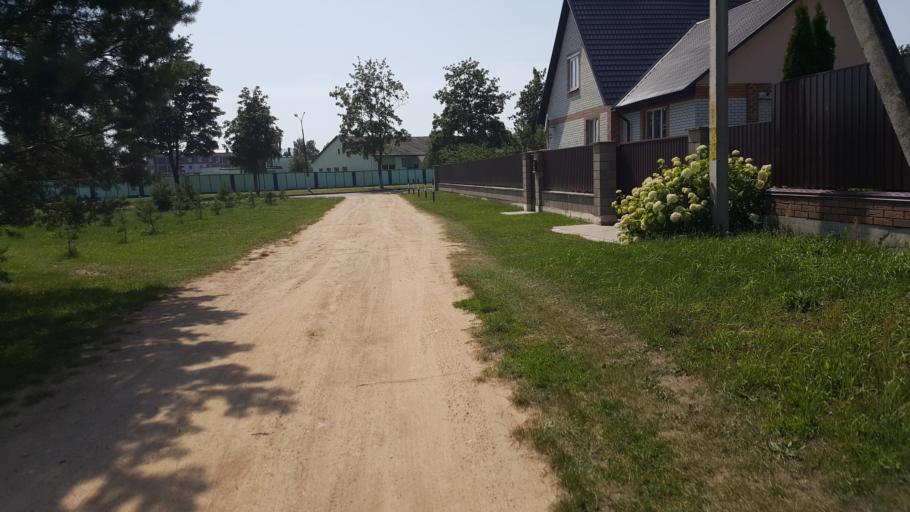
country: BY
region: Brest
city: Zhabinka
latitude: 52.1990
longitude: 24.0313
